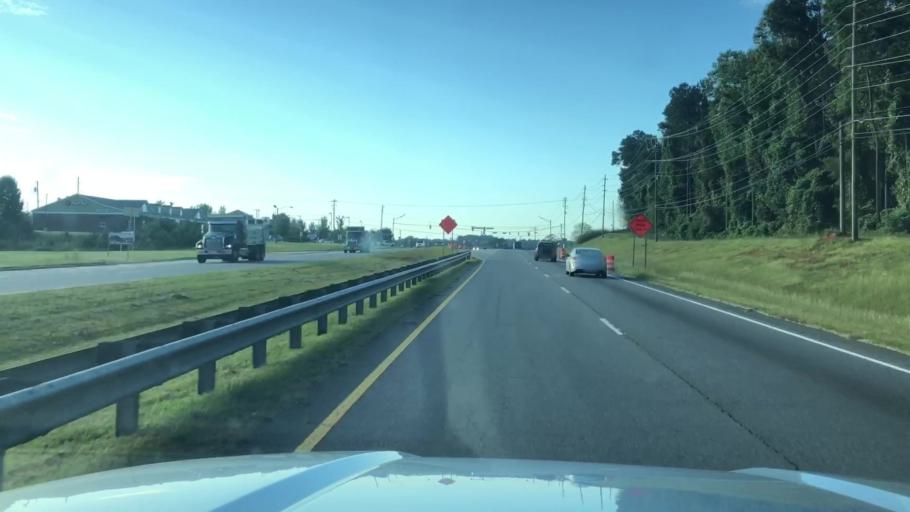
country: US
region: Georgia
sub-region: Cobb County
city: Acworth
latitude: 34.0667
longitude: -84.7248
